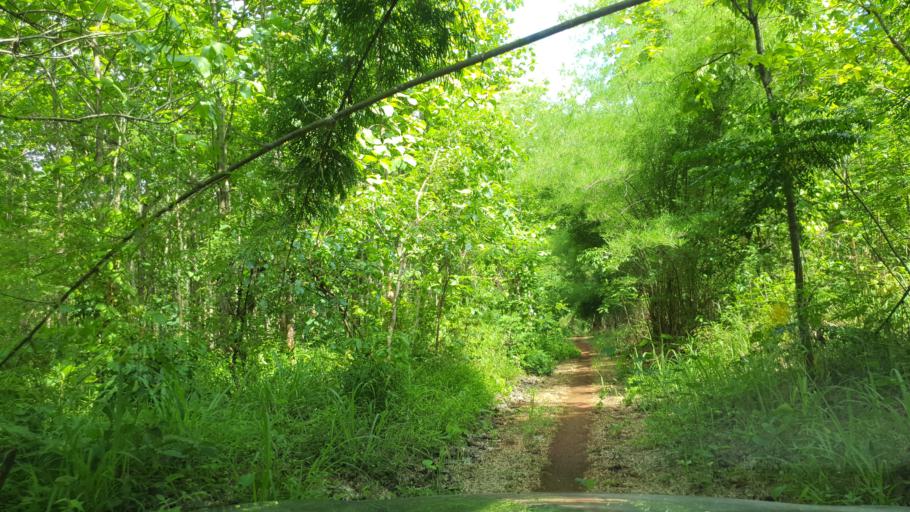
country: TH
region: Chiang Mai
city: Mae Taeng
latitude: 19.0765
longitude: 99.0975
